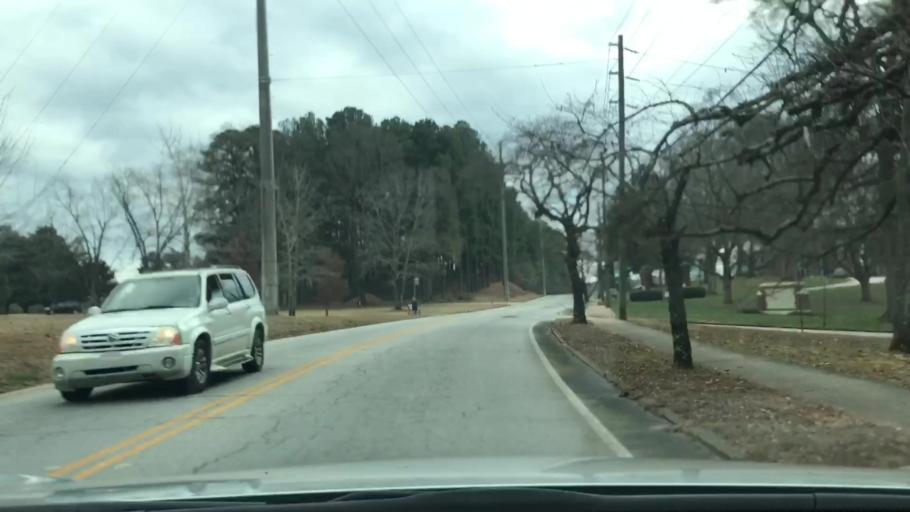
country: US
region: Georgia
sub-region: DeKalb County
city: Avondale Estates
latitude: 33.7657
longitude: -84.2807
